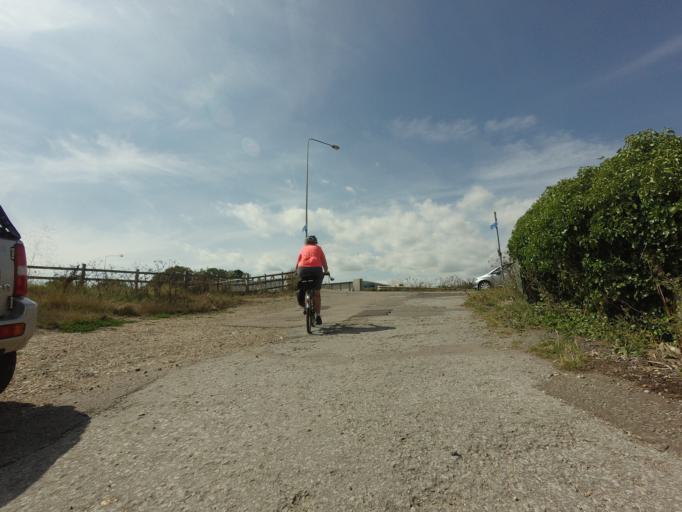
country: GB
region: England
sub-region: East Sussex
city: Rye
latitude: 50.9531
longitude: 0.7398
